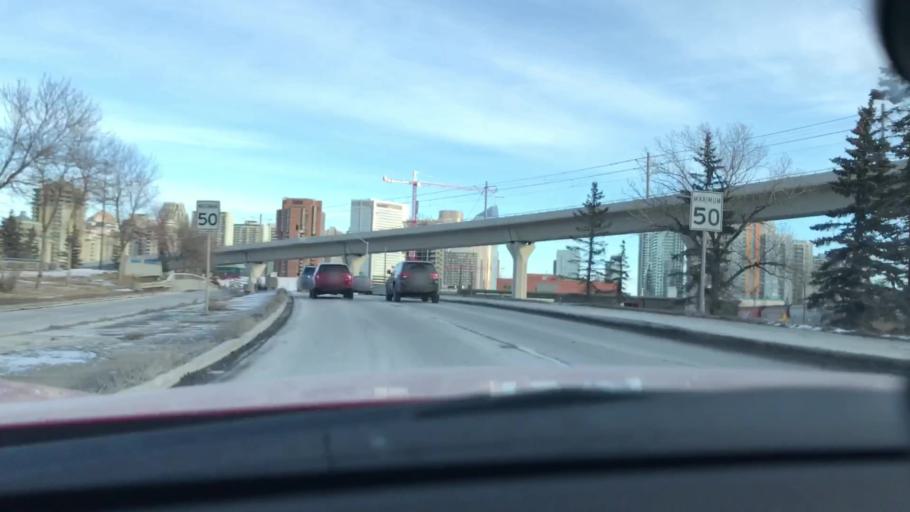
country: CA
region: Alberta
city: Calgary
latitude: 51.0453
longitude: -114.0958
